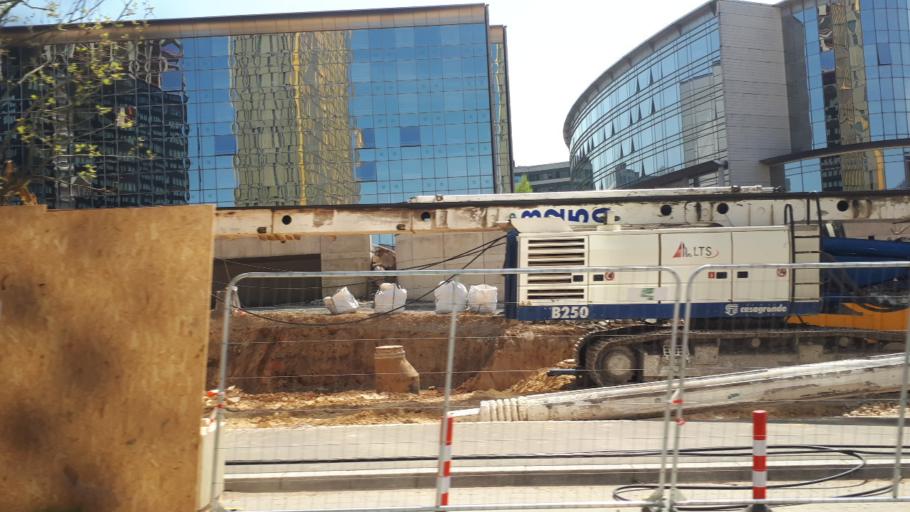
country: LU
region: Luxembourg
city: Kirchberg
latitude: 49.6214
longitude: 6.1440
